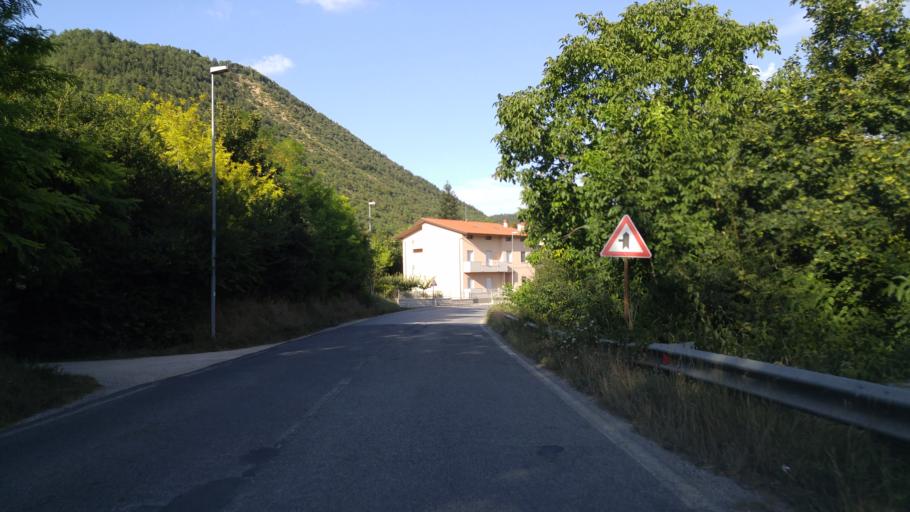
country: IT
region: The Marches
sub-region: Provincia di Pesaro e Urbino
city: Acqualagna
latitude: 43.6130
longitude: 12.6456
